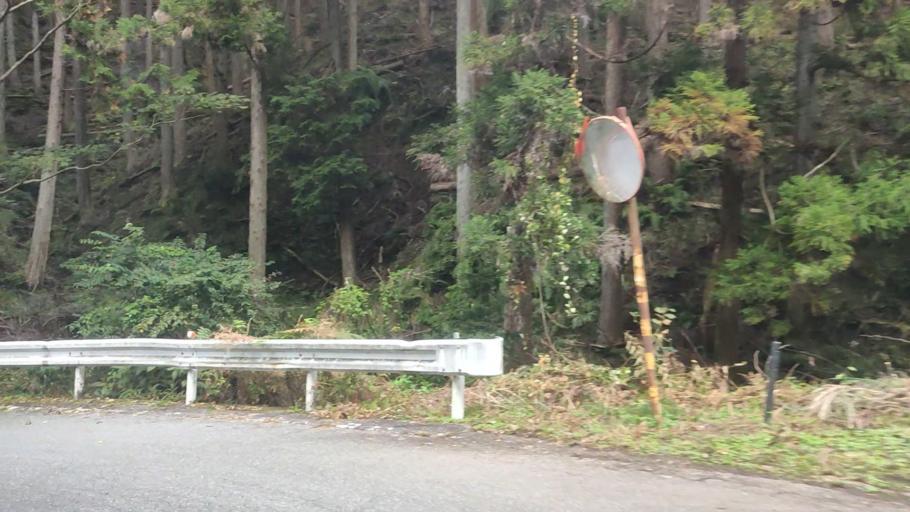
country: JP
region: Shizuoka
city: Ito
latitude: 34.9543
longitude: 139.0435
